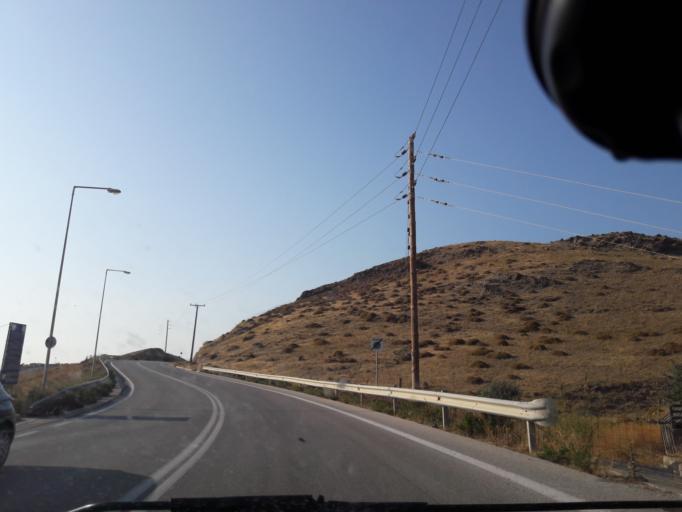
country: GR
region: North Aegean
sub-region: Nomos Lesvou
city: Myrina
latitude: 39.8650
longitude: 25.0563
